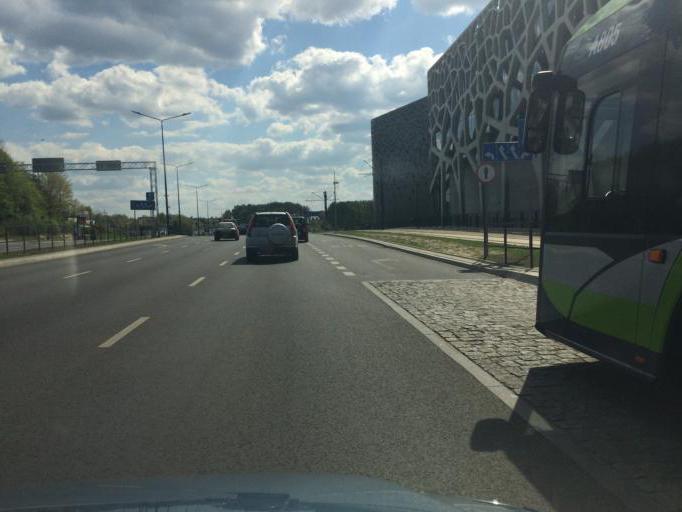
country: PL
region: Warmian-Masurian Voivodeship
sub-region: Powiat olsztynski
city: Olsztyn
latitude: 53.7547
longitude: 20.4860
